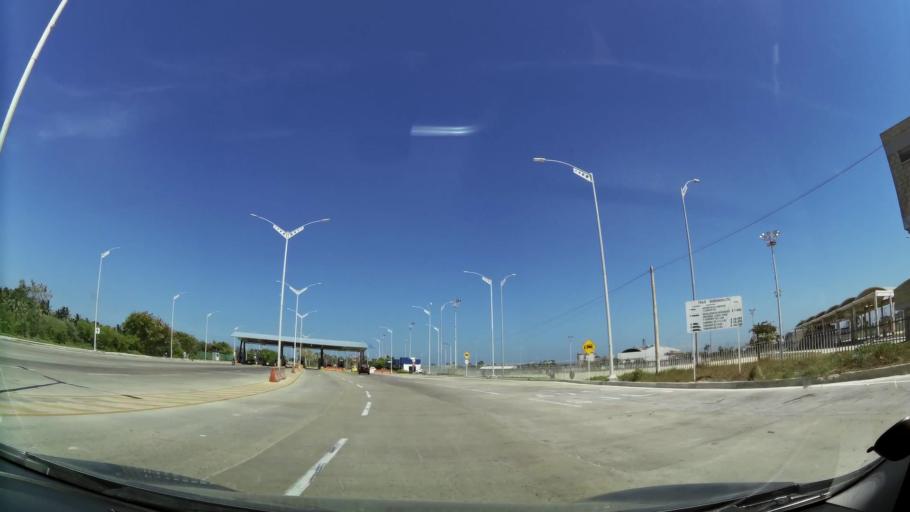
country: CO
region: Atlantico
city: Barranquilla
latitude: 10.9854
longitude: -74.7728
